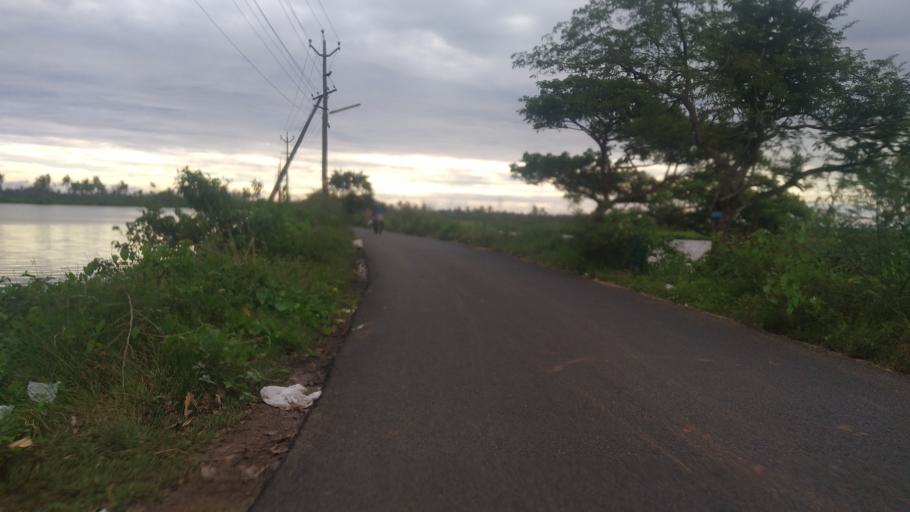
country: IN
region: Kerala
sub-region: Alappuzha
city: Arukutti
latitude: 9.8586
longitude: 76.2785
